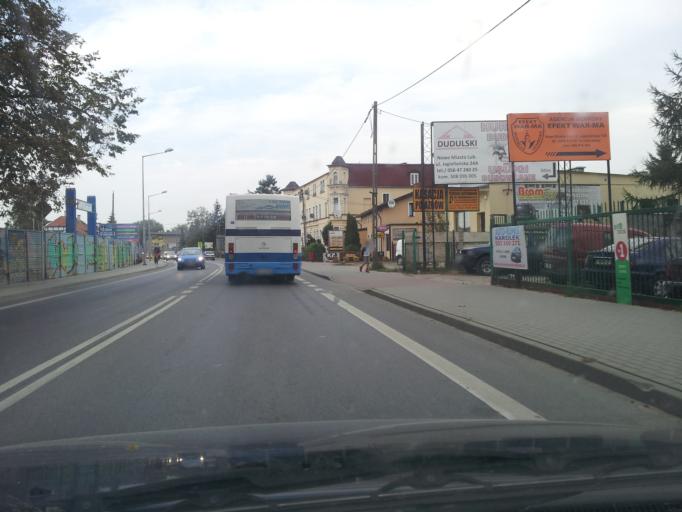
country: PL
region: Warmian-Masurian Voivodeship
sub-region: Powiat nowomiejski
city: Nowe Miasto Lubawskie
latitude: 53.4184
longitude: 19.5943
